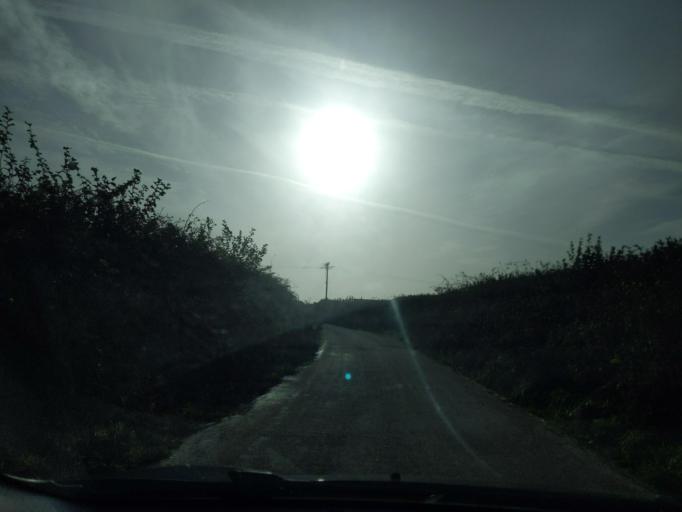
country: GB
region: England
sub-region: Cornwall
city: Pillaton
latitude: 50.3695
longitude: -4.2965
